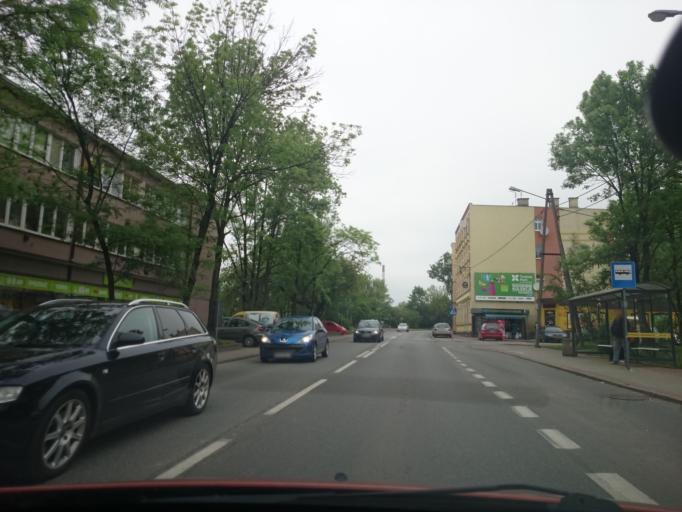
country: PL
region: Opole Voivodeship
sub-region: Powiat opolski
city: Opole
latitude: 50.6757
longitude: 17.9233
